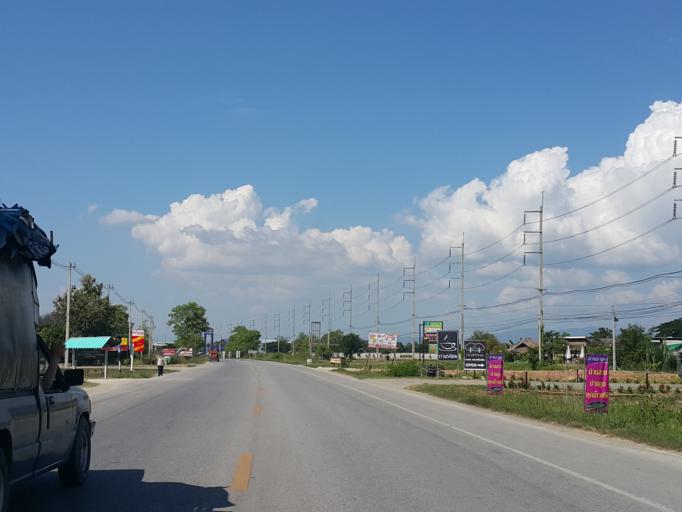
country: TH
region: Chiang Mai
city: San Sai
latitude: 18.7904
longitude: 99.0687
